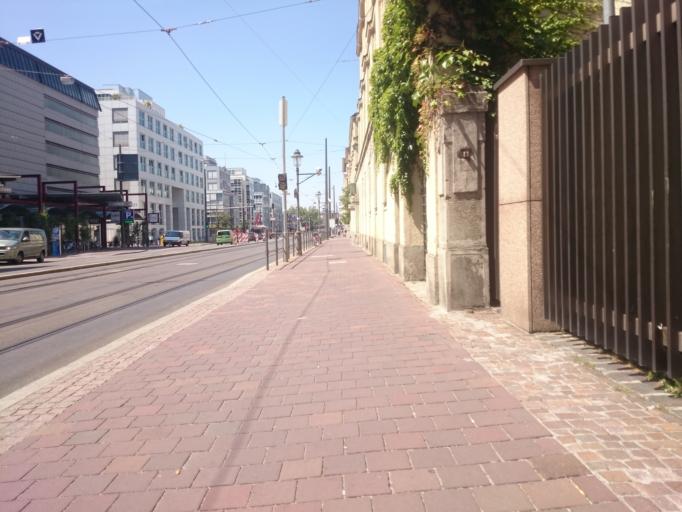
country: DE
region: Bavaria
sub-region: Swabia
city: Augsburg
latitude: 48.3650
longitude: 10.8923
